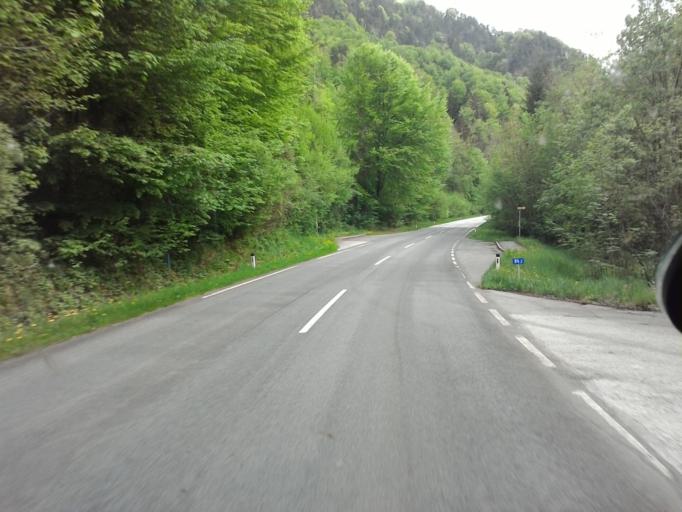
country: AT
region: Styria
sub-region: Politischer Bezirk Liezen
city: Altenmarkt bei Sankt Gallen
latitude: 47.7060
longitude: 14.6904
